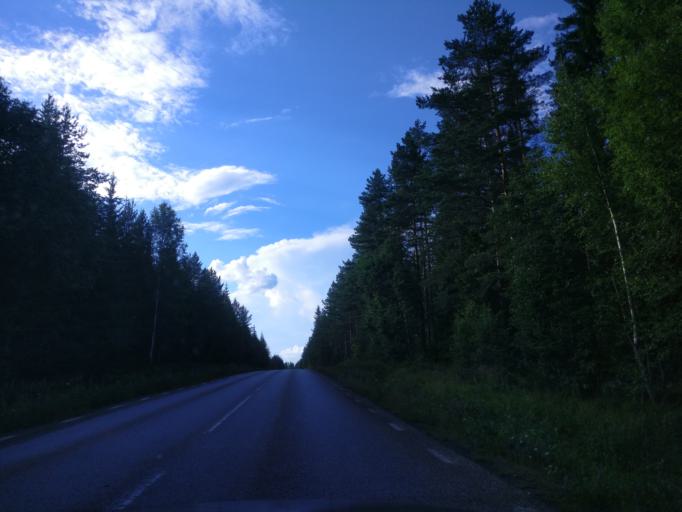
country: SE
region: Dalarna
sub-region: Ludvika Kommun
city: Ludvika
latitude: 60.2867
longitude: 15.1409
